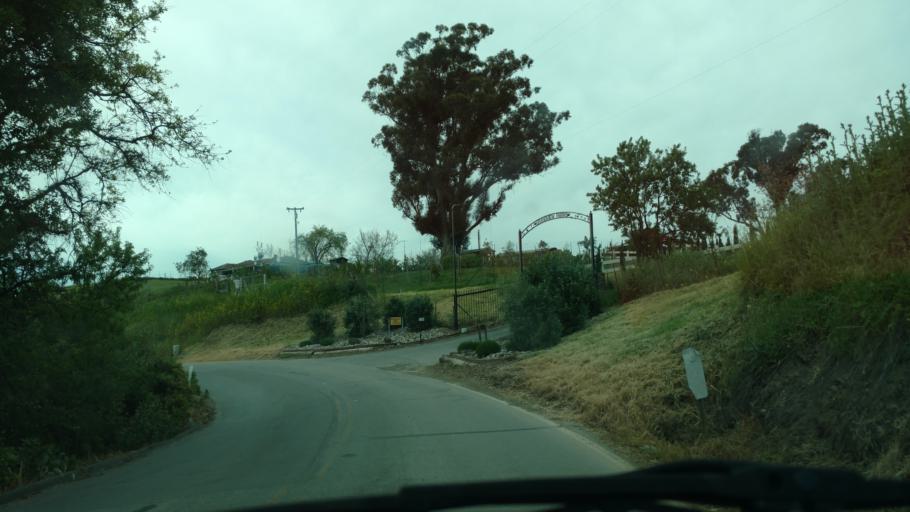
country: US
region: California
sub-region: Santa Clara County
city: East Foothills
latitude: 37.3665
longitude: -121.7653
